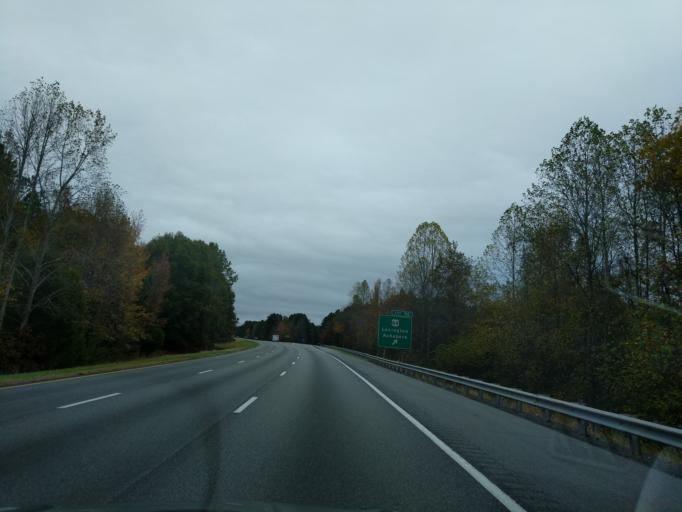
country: US
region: North Carolina
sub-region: Davidson County
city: Lexington
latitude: 35.8055
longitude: -80.1864
